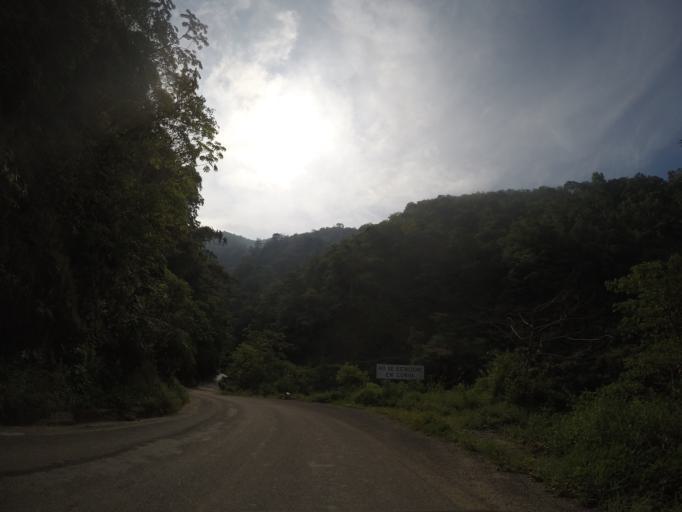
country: MX
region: Oaxaca
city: Pluma Hidalgo
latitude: 15.9397
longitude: -96.4314
